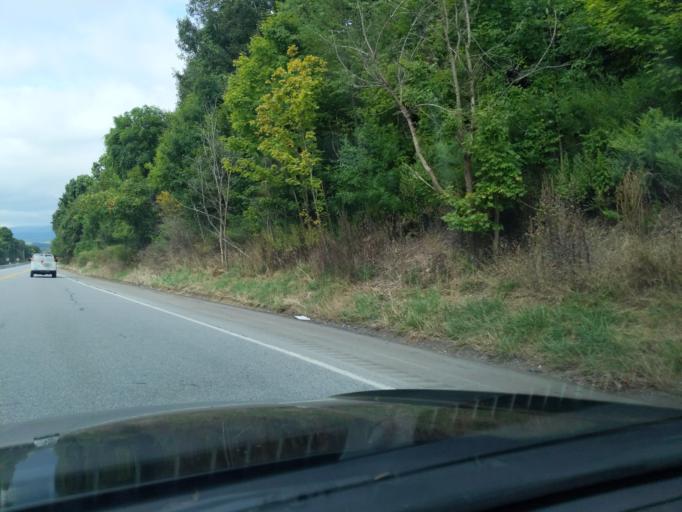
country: US
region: Pennsylvania
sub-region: Blair County
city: Hollidaysburg
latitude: 40.4086
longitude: -78.4004
